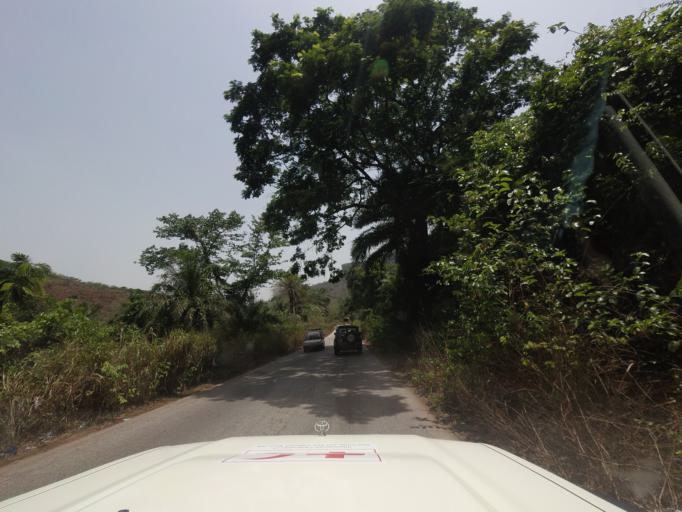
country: GN
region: Kindia
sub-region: Coyah
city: Coyah
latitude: 9.7392
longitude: -13.3705
